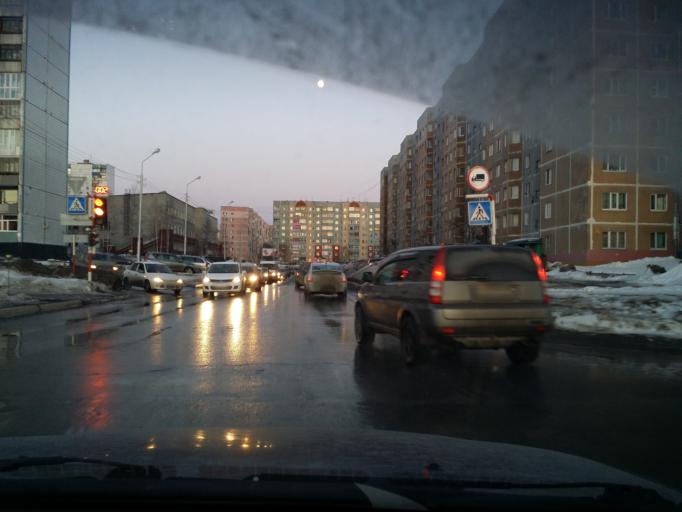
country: RU
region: Khanty-Mansiyskiy Avtonomnyy Okrug
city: Nizhnevartovsk
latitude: 60.9324
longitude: 76.5882
